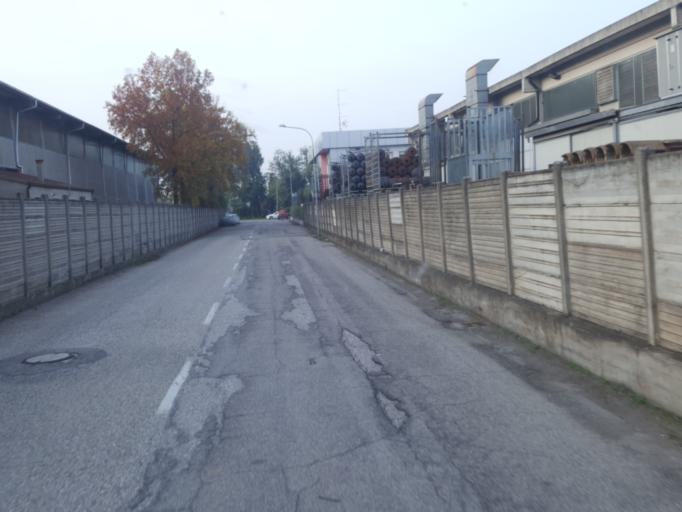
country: IT
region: Veneto
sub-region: Provincia di Verona
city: Zevio
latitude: 45.3708
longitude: 11.0941
